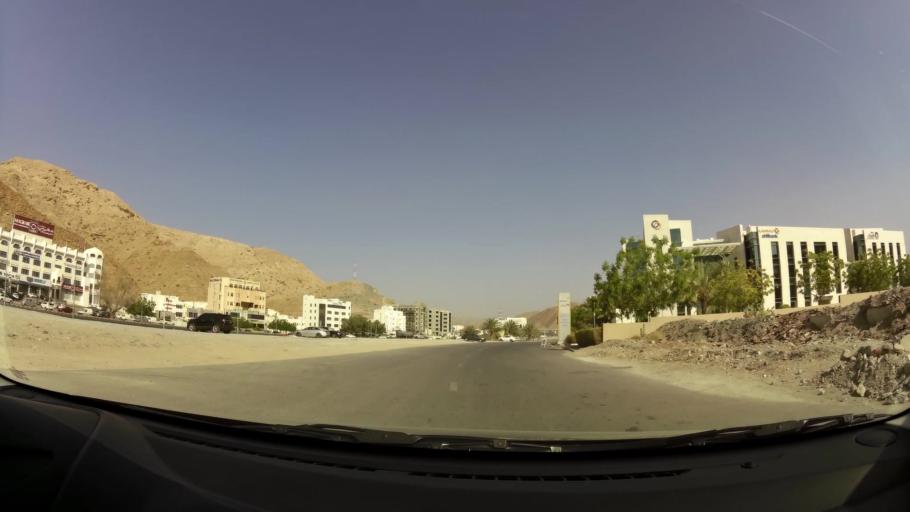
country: OM
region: Muhafazat Masqat
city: Muscat
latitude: 23.5995
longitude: 58.5181
